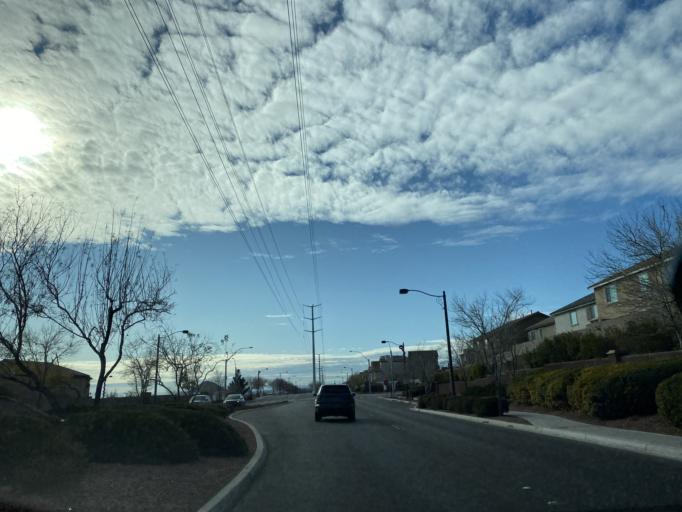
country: US
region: Nevada
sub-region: Clark County
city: Summerlin South
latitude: 36.2894
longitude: -115.3289
